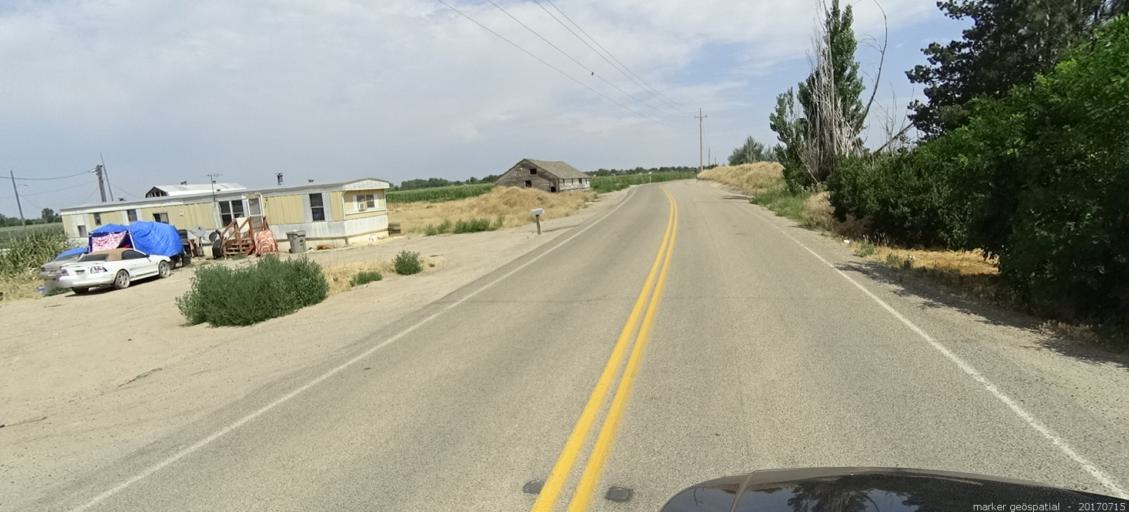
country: US
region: Idaho
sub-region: Ada County
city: Garden City
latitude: 43.5365
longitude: -116.2742
